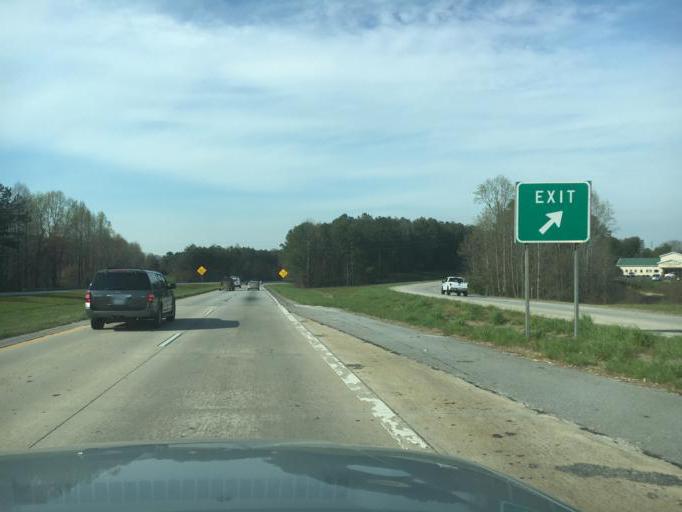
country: US
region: Georgia
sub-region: Habersham County
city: Cornelia
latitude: 34.5337
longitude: -83.5406
